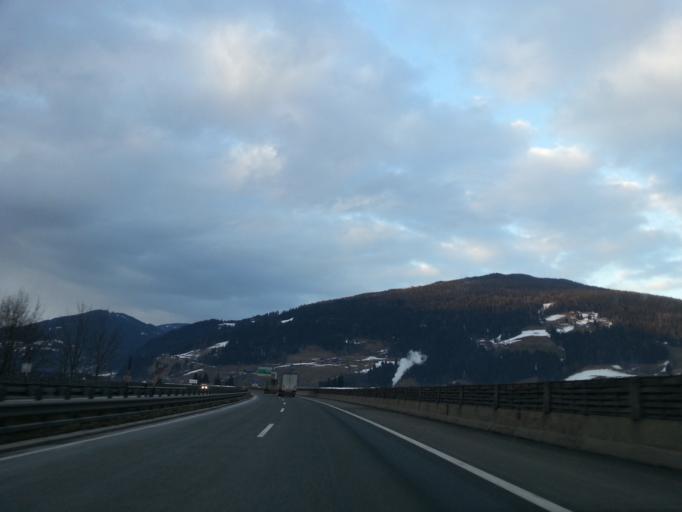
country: AT
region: Salzburg
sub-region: Politischer Bezirk Sankt Johann im Pongau
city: Altenmarkt im Pongau
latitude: 47.3799
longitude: 13.4011
